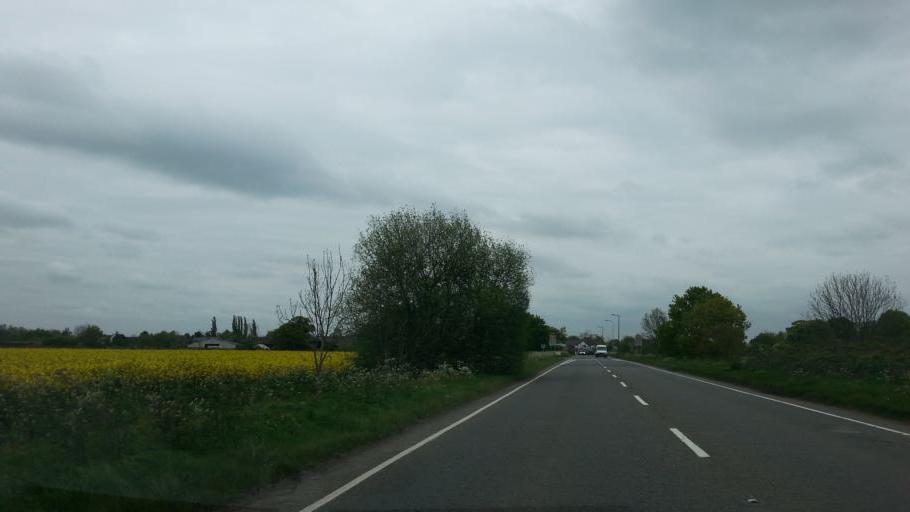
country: GB
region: England
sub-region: Lincolnshire
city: Bourne
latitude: 52.7342
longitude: -0.3675
